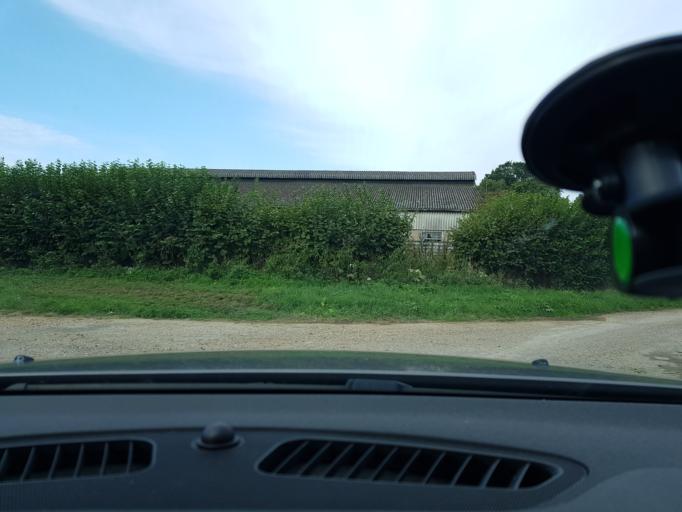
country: GB
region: England
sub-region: West Berkshire
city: Hungerford
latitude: 51.3884
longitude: -1.5074
